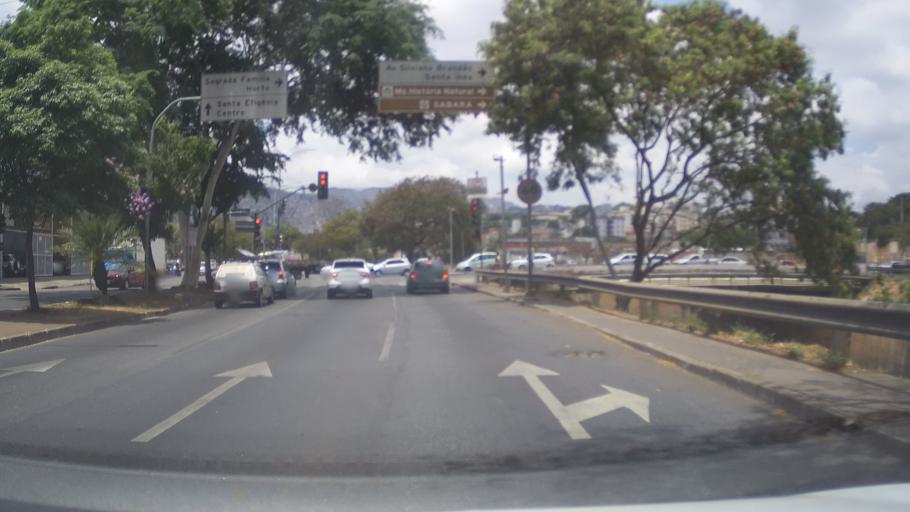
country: BR
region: Minas Gerais
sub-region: Belo Horizonte
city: Belo Horizonte
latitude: -19.9068
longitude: -43.9106
